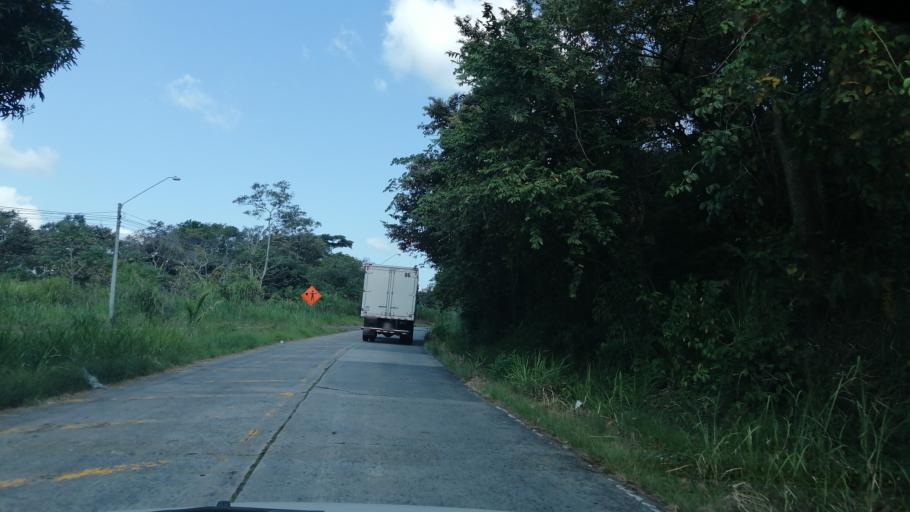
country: PA
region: Panama
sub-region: Distrito de Panama
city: Ancon
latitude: 8.9350
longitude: -79.5735
